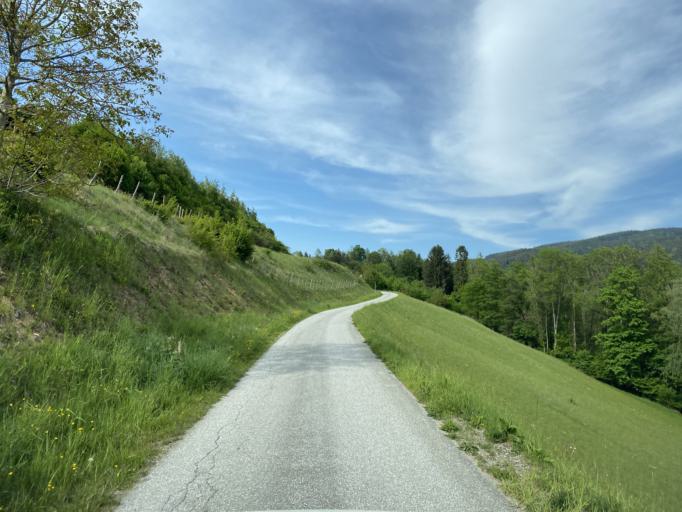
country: AT
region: Styria
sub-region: Politischer Bezirk Weiz
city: Koglhof
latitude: 47.3016
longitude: 15.6859
